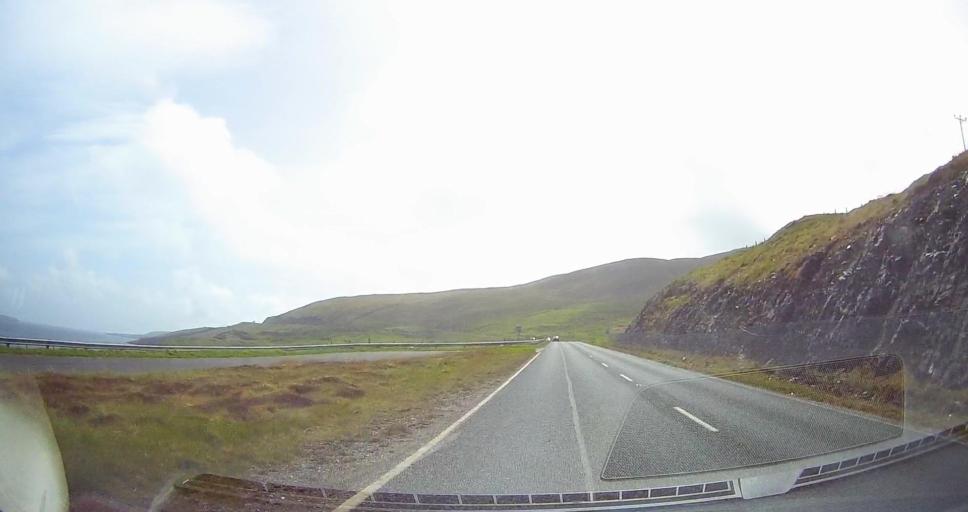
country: GB
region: Scotland
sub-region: Shetland Islands
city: Sandwick
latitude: 60.0301
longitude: -1.2353
